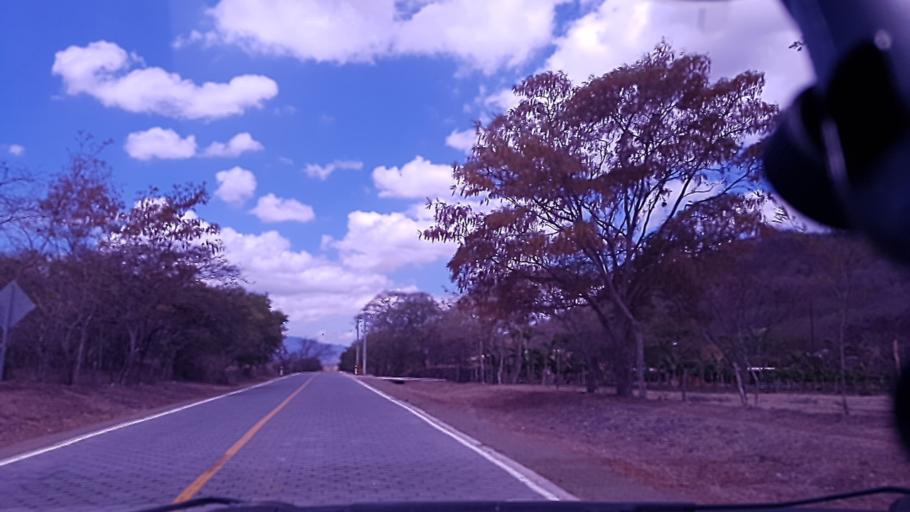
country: NI
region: Esteli
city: Condega
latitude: 13.3807
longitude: -86.3568
